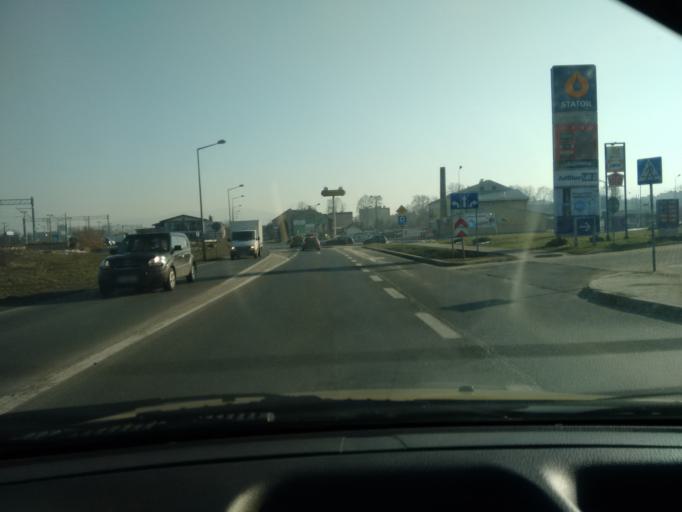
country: PL
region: Lesser Poland Voivodeship
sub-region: Powiat wadowicki
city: Wadowice
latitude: 49.8871
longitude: 19.4991
